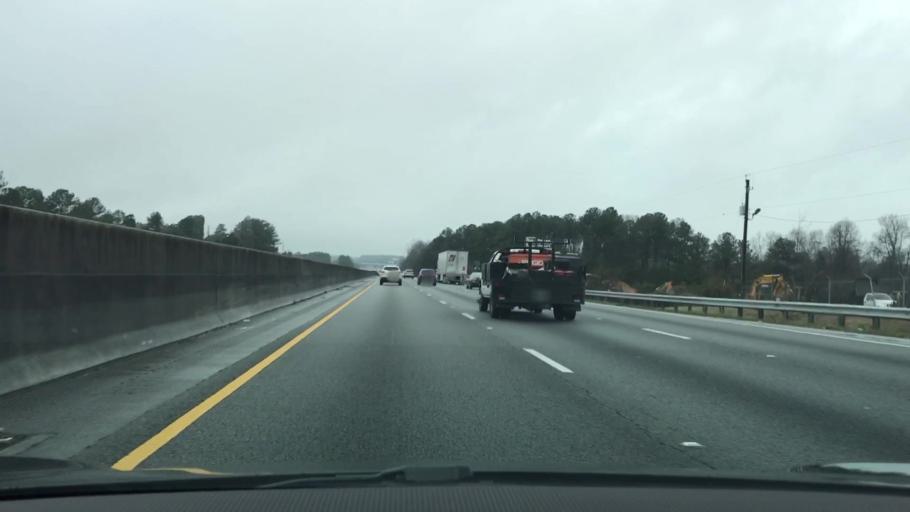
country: US
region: Georgia
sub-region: DeKalb County
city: Lithonia
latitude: 33.6915
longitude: -84.0719
